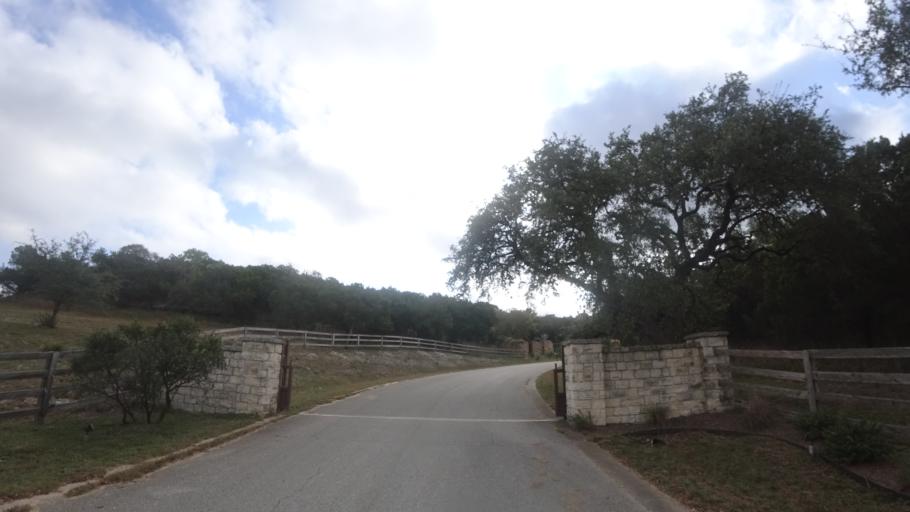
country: US
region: Texas
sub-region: Travis County
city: Barton Creek
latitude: 30.3063
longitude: -97.8970
